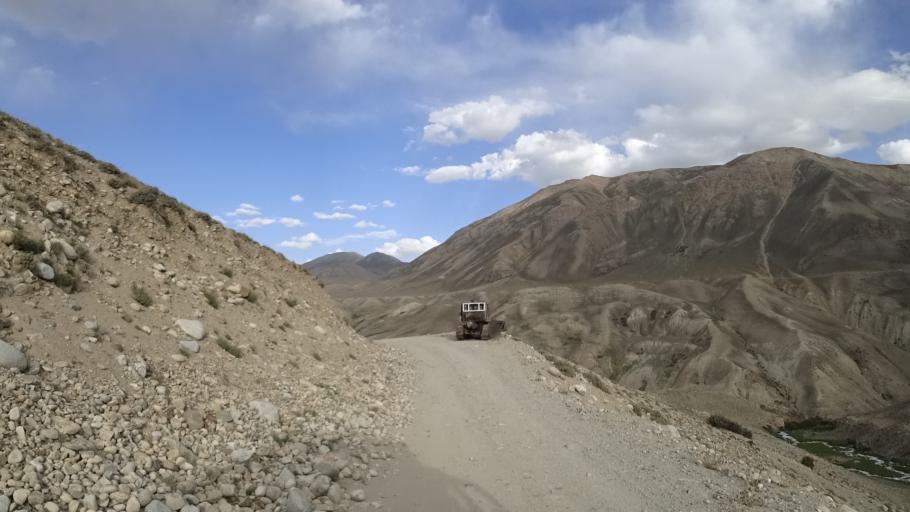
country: AF
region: Badakhshan
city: Khandud
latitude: 37.2219
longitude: 72.7928
